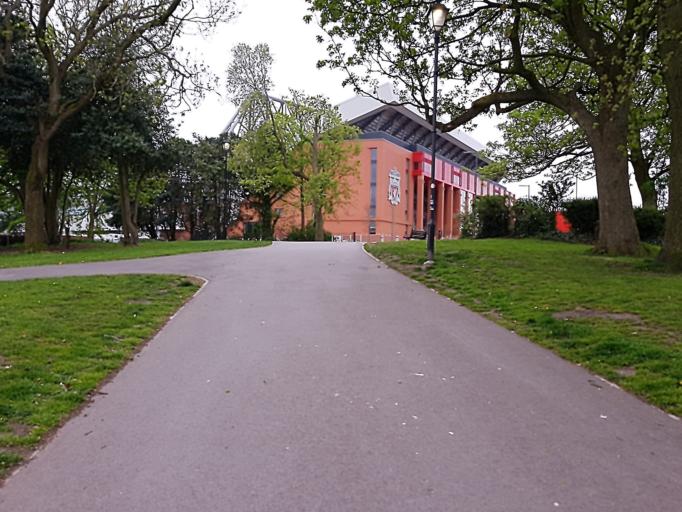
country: GB
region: England
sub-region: Liverpool
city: Liverpool
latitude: 53.4330
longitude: -2.9610
